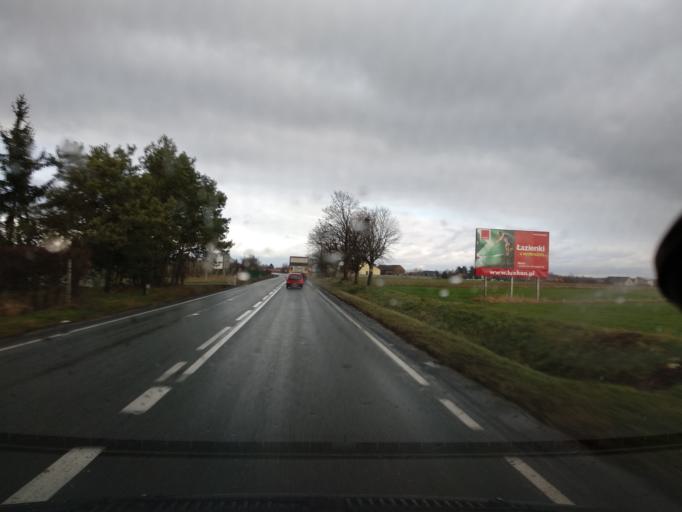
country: PL
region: Greater Poland Voivodeship
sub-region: Powiat koninski
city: Stare Miasto
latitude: 52.1507
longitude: 18.2027
